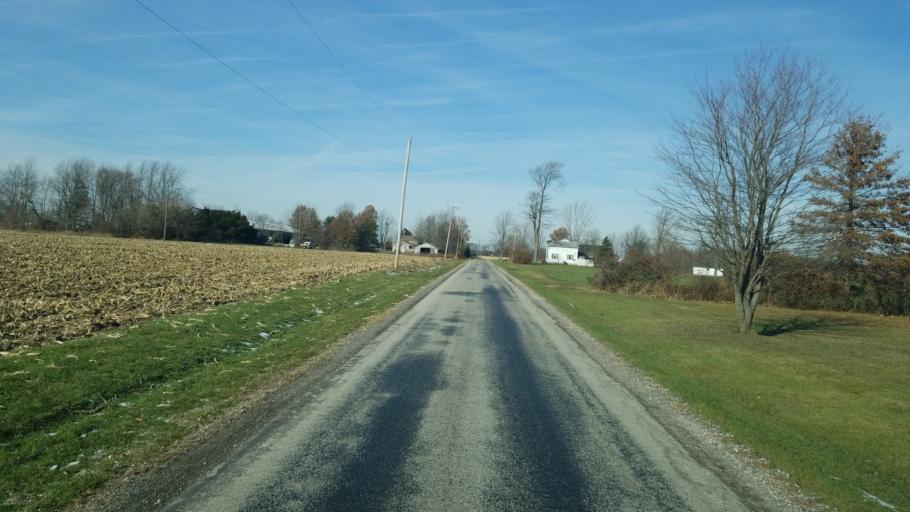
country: US
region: Ohio
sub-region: Huron County
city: Wakeman
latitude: 41.2363
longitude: -82.4207
